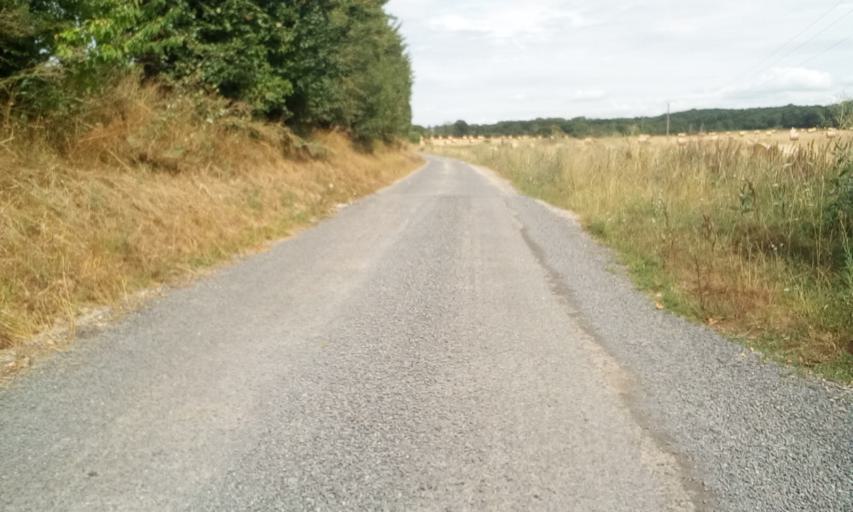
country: FR
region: Lower Normandy
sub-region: Departement du Calvados
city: Herouvillette
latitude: 49.2172
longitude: -0.2424
